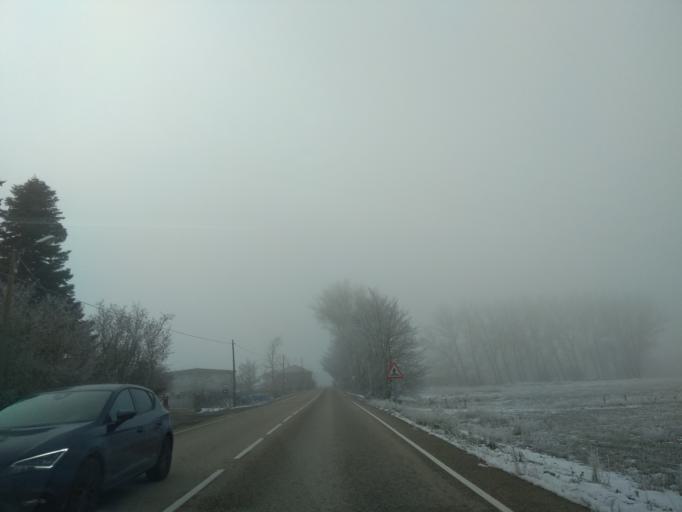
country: ES
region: Castille and Leon
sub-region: Provincia de Burgos
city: Espinosa de los Monteros
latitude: 43.0427
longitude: -3.4911
